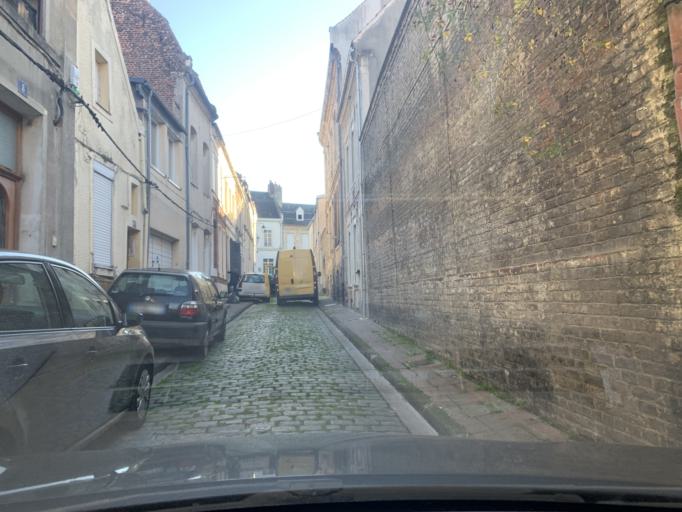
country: FR
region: Nord-Pas-de-Calais
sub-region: Departement du Nord
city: Neuville-Saint-Remy
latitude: 50.1790
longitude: 3.2317
